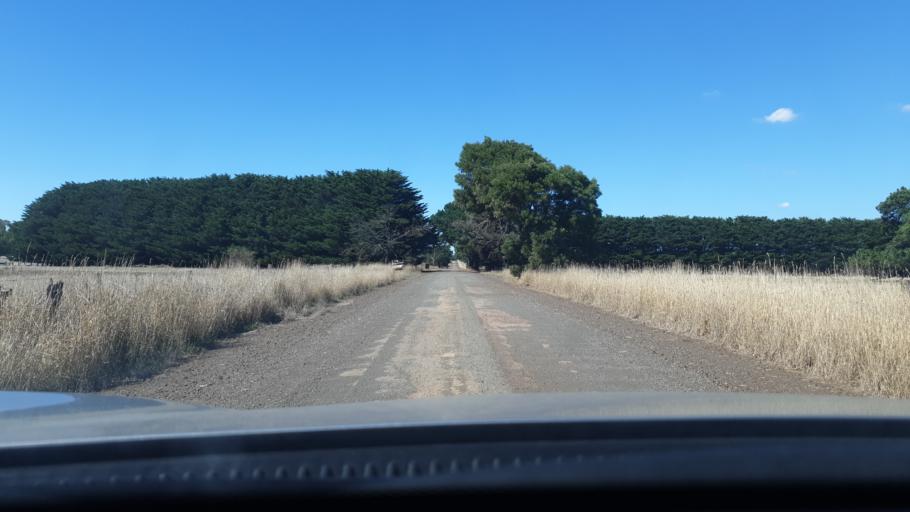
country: AU
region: Victoria
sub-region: Warrnambool
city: Warrnambool
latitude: -38.1650
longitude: 142.3744
